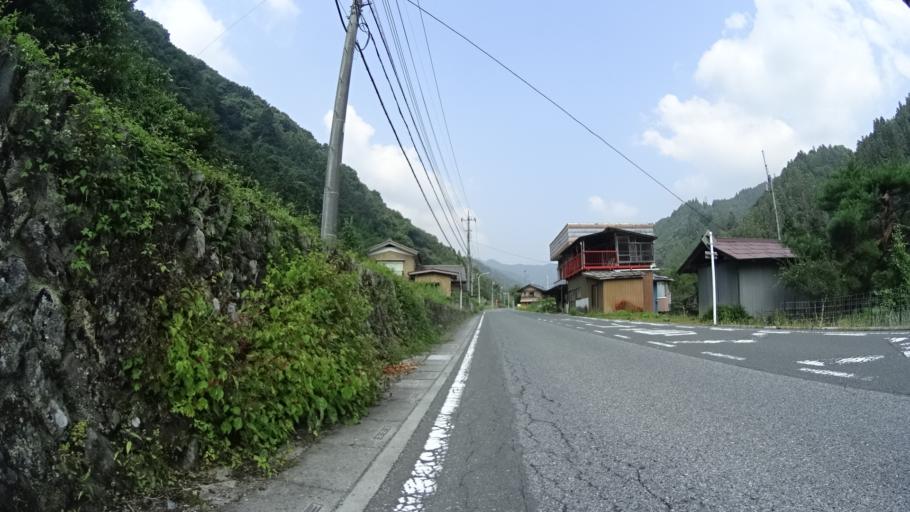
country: JP
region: Saitama
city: Chichibu
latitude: 36.0483
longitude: 138.8845
